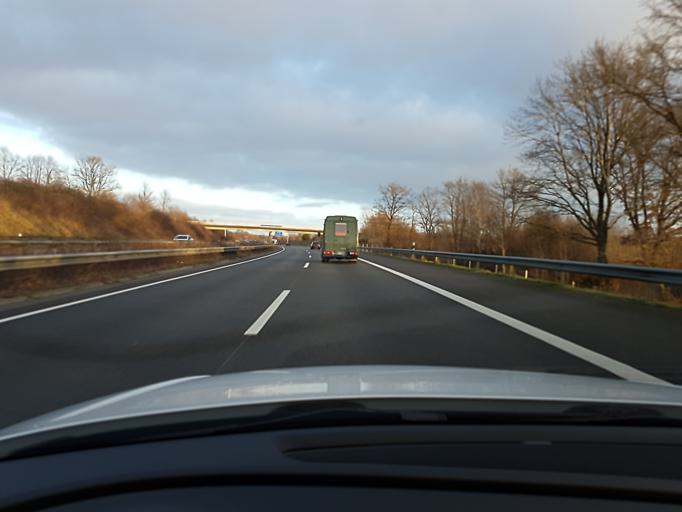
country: DE
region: Schleswig-Holstein
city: Hamberge
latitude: 53.8326
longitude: 10.6226
